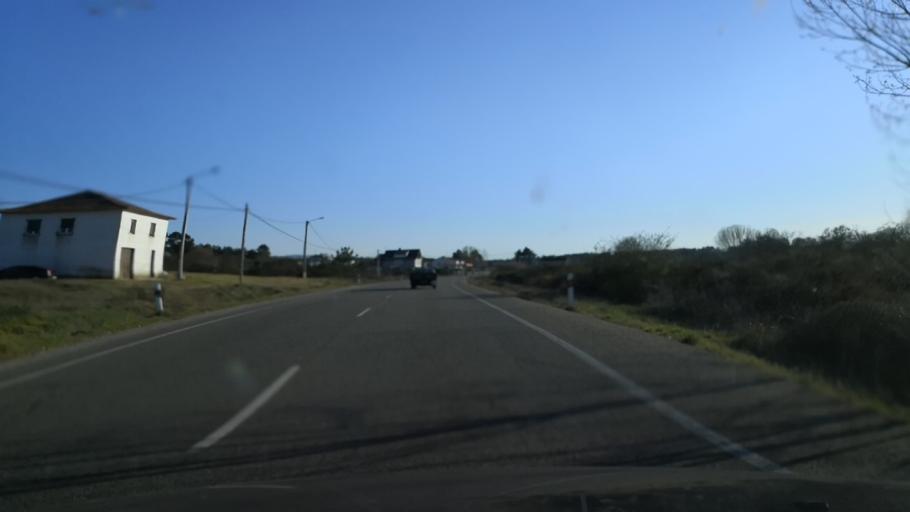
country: ES
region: Galicia
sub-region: Provincia de Ourense
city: Oimbra
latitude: 41.8282
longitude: -7.4241
